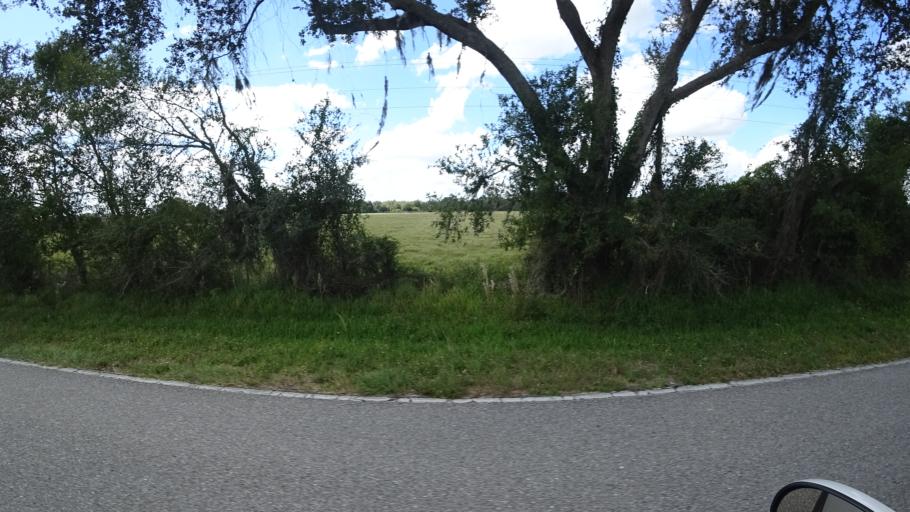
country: US
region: Florida
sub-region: Sarasota County
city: Lake Sarasota
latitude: 27.3254
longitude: -82.1667
